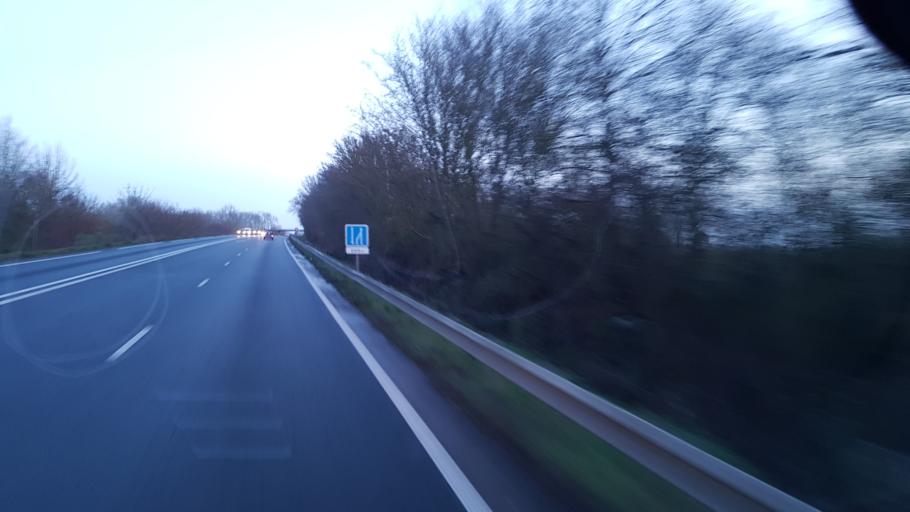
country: FR
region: Nord-Pas-de-Calais
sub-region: Departement du Nord
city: Lambres-lez-Douai
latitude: 50.3454
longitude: 3.0724
